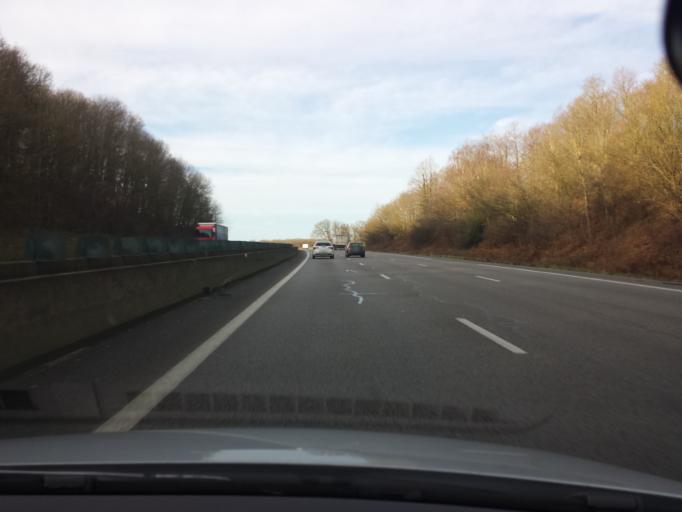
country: FR
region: Ile-de-France
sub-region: Departement des Yvelines
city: Bonnieres-sur-Seine
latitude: 49.0199
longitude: 1.5771
